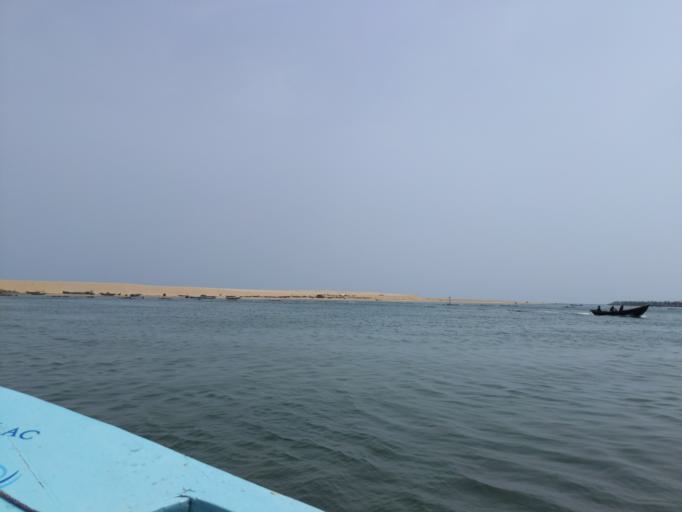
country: BJ
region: Littoral
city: Cotonou
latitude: 6.3582
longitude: 2.4437
